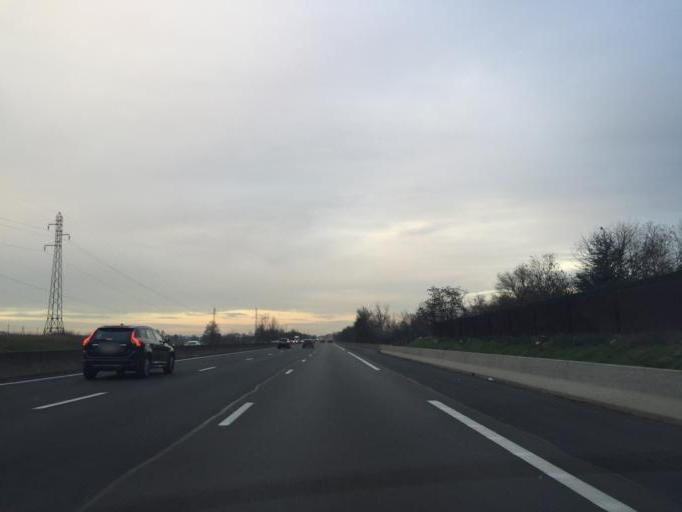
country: FR
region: Bourgogne
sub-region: Departement de Saone-et-Loire
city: La Chapelle-de-Guinchay
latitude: 46.2099
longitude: 4.7840
